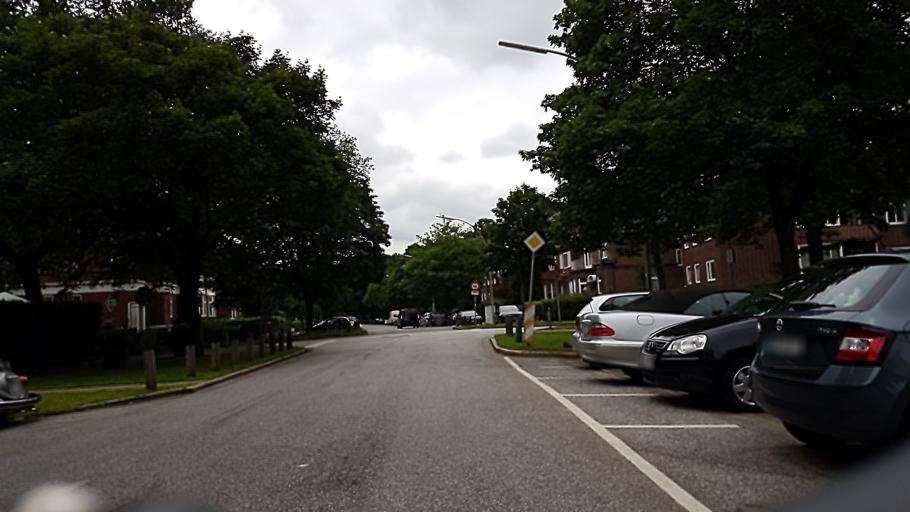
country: DE
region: Hamburg
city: Hamburg-Nord
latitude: 53.5882
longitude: 9.9957
